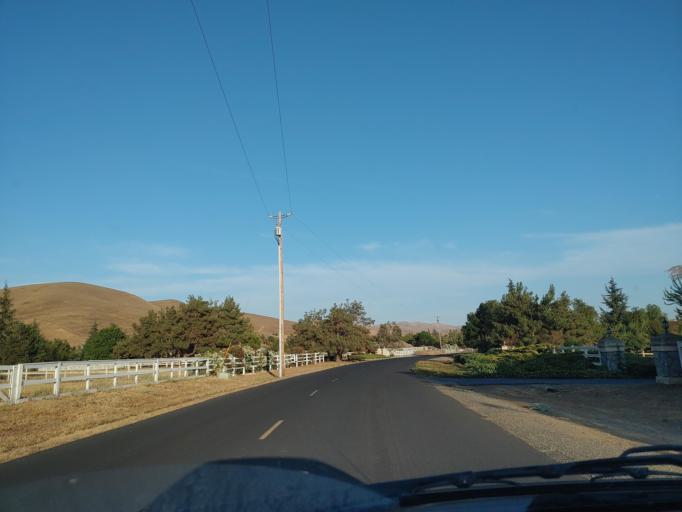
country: US
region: California
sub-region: San Benito County
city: Ridgemark
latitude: 36.7982
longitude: -121.3284
